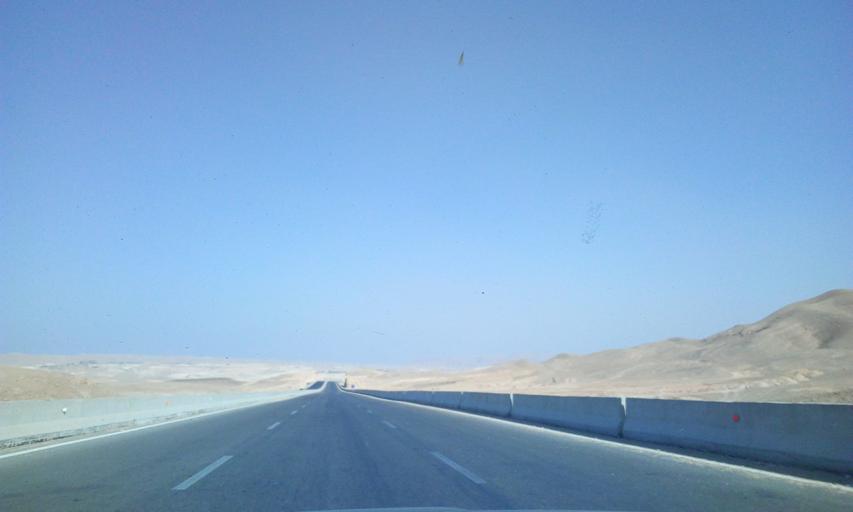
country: EG
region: As Suways
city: Ain Sukhna
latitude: 29.4432
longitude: 32.3602
